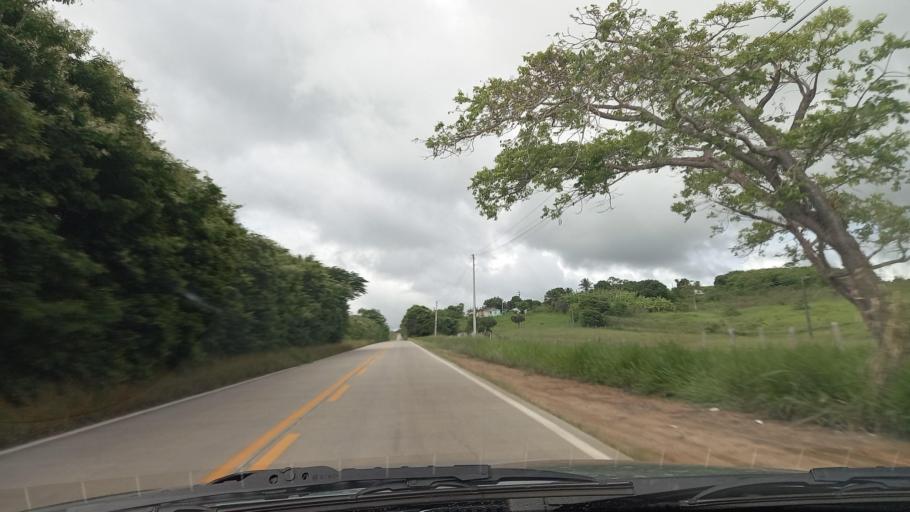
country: BR
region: Pernambuco
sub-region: Quipapa
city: Quipapa
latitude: -8.8045
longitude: -36.0059
